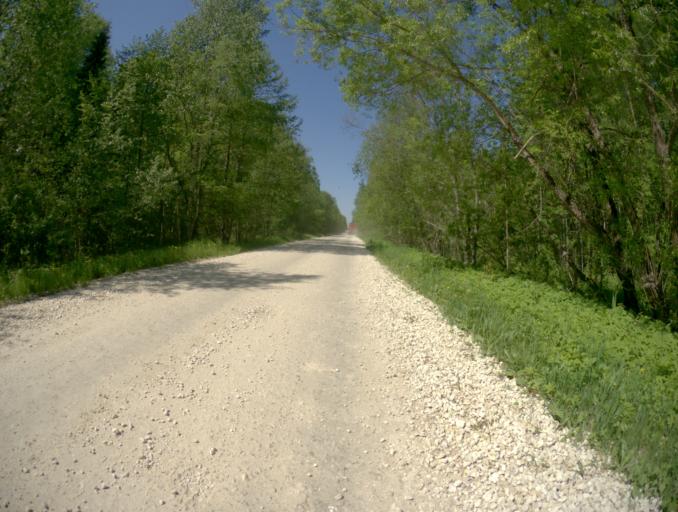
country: RU
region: Vladimir
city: Anopino
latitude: 55.7086
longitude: 40.6516
